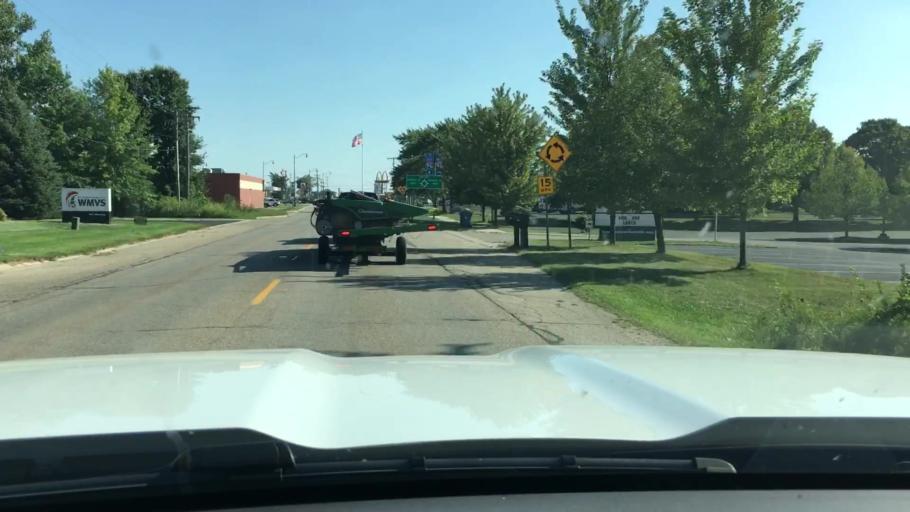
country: US
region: Michigan
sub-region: Ottawa County
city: Coopersville
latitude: 43.0622
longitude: -85.9569
